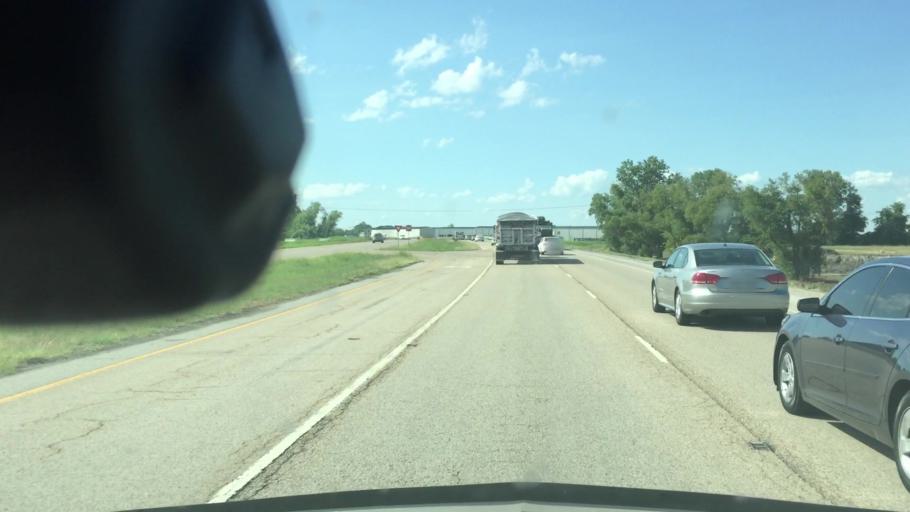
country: US
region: Illinois
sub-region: Saint Clair County
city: East Saint Louis
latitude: 38.6542
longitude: -90.1335
